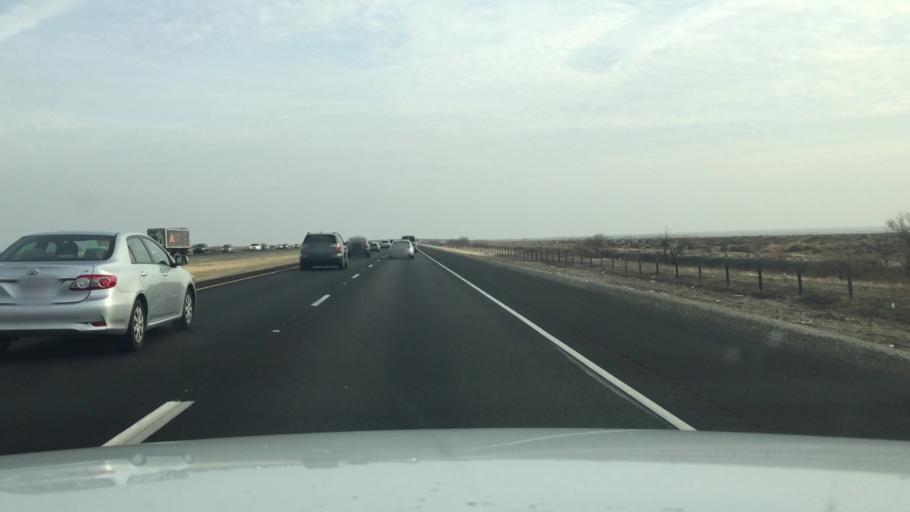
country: US
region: California
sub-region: Kern County
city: Lost Hills
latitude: 35.7173
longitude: -119.7287
